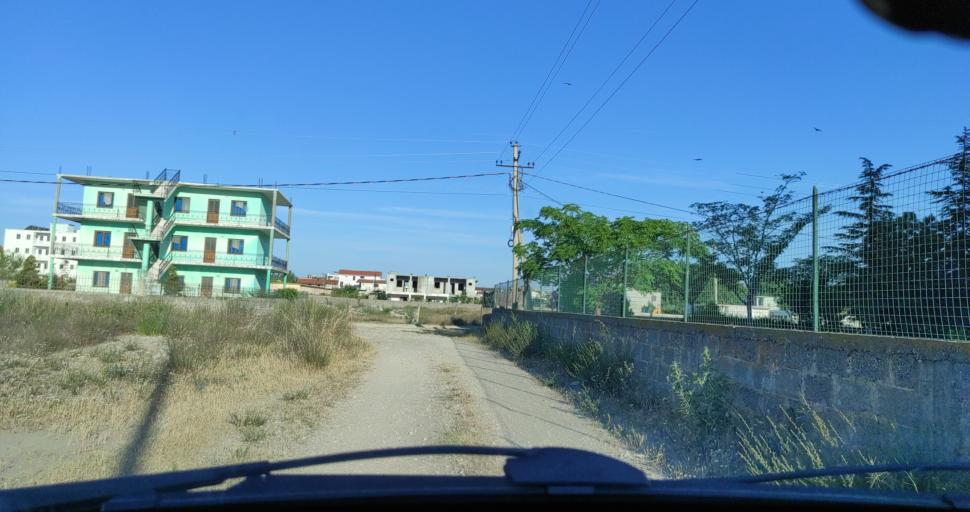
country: AL
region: Shkoder
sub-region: Rrethi i Shkodres
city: Velipoje
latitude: 41.8666
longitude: 19.4360
